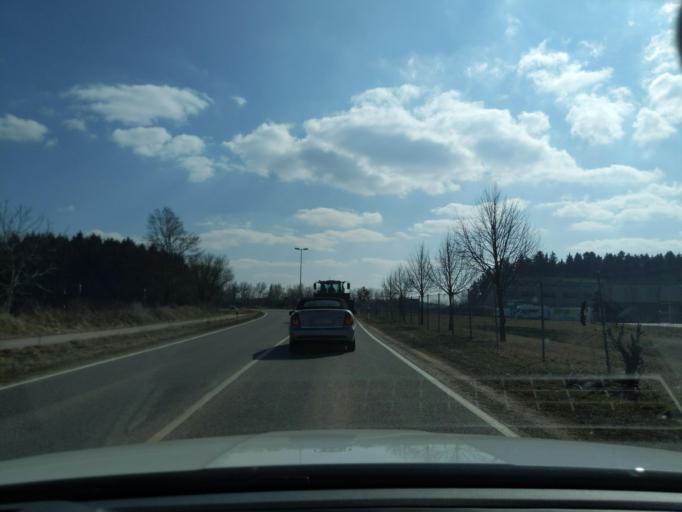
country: DE
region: Bavaria
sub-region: Swabia
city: Vohringen
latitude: 48.3232
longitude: 10.0963
